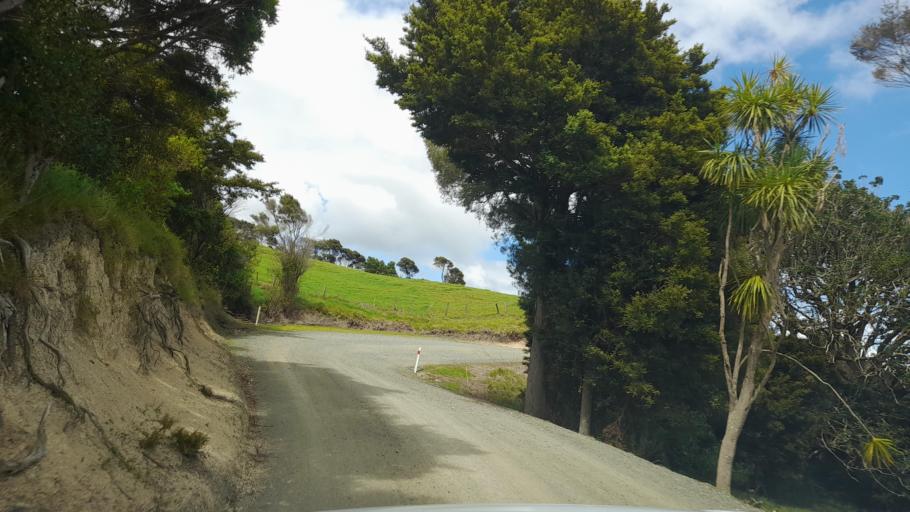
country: NZ
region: Auckland
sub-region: Auckland
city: Wellsford
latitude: -36.2082
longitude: 174.3344
